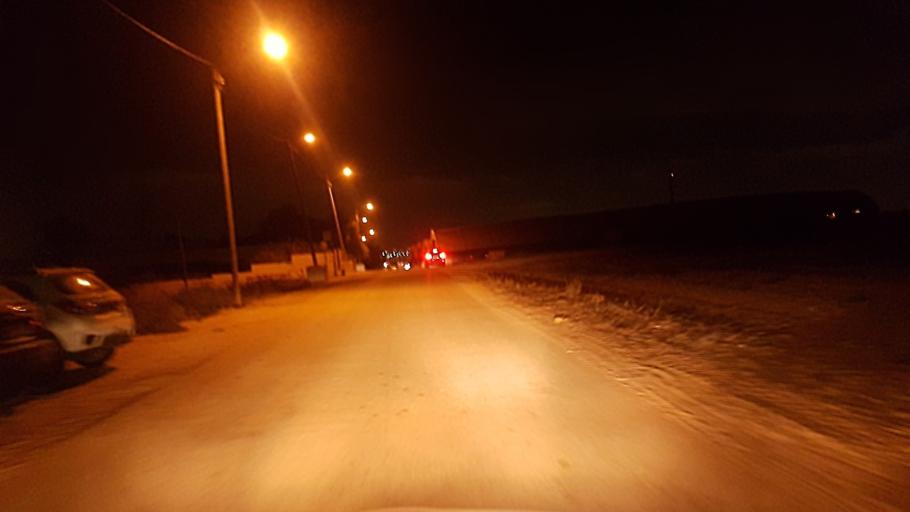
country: IL
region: Central District
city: Hod HaSharon
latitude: 32.1593
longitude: 34.8723
